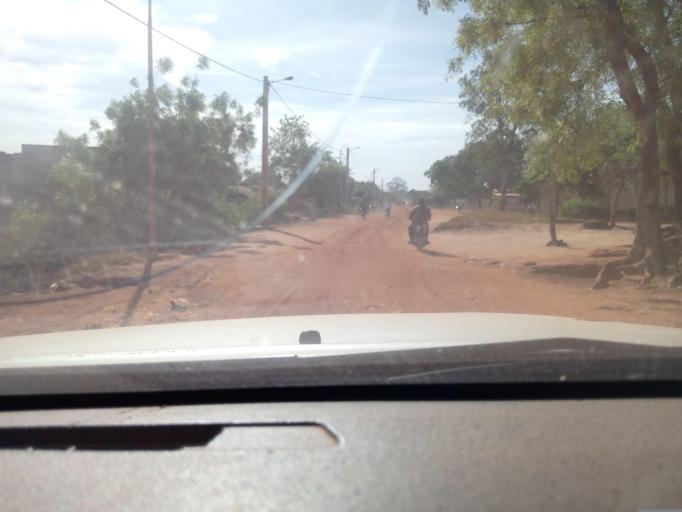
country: ML
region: Sikasso
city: Sikasso
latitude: 11.8490
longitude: -6.0153
